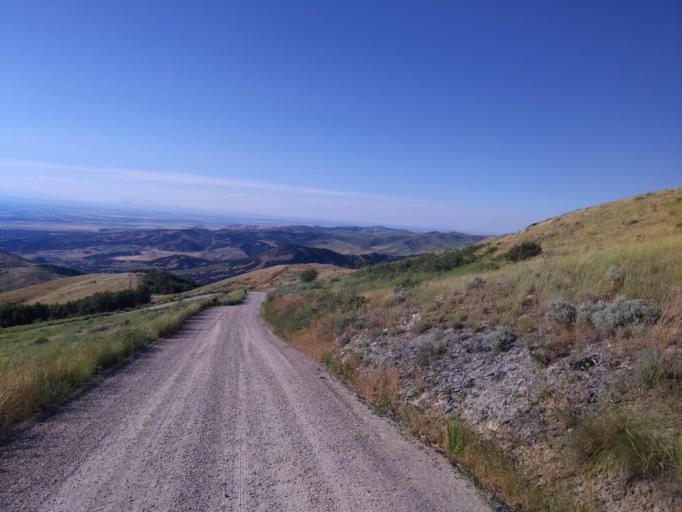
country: US
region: Idaho
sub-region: Bannock County
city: Pocatello
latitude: 42.8505
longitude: -112.3622
